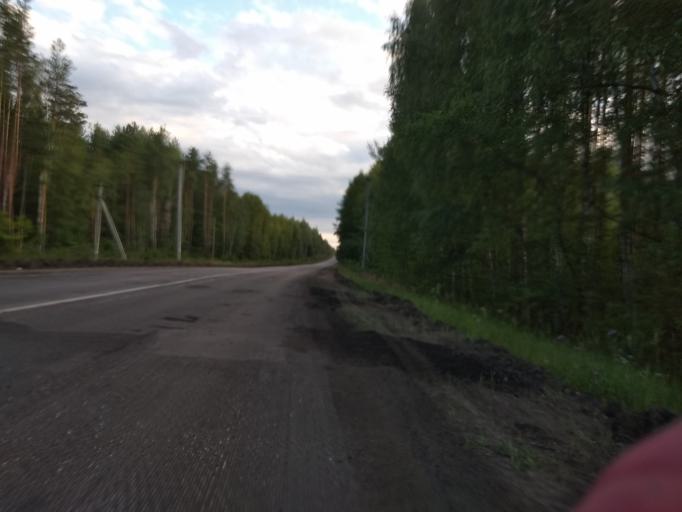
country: RU
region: Moskovskaya
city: Misheronskiy
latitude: 55.6437
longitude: 39.7565
